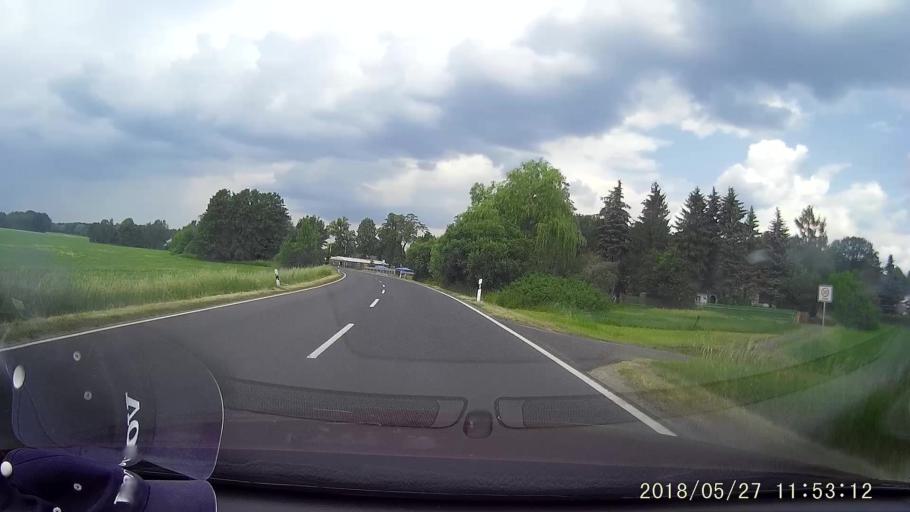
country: DE
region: Saxony
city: Quitzdorf
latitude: 51.3031
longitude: 14.7739
